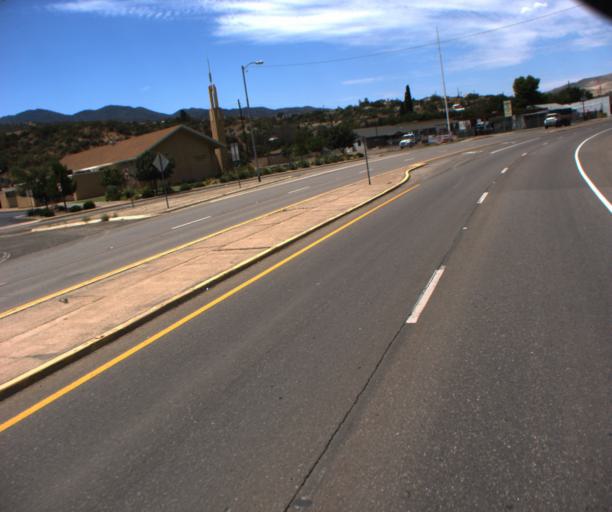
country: US
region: Arizona
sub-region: Gila County
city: Claypool
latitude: 33.4111
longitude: -110.8436
